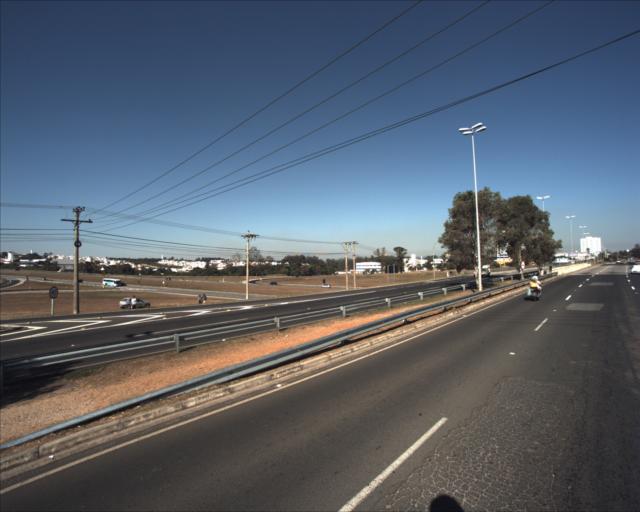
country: BR
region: Sao Paulo
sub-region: Sorocaba
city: Sorocaba
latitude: -23.4684
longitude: -47.4242
